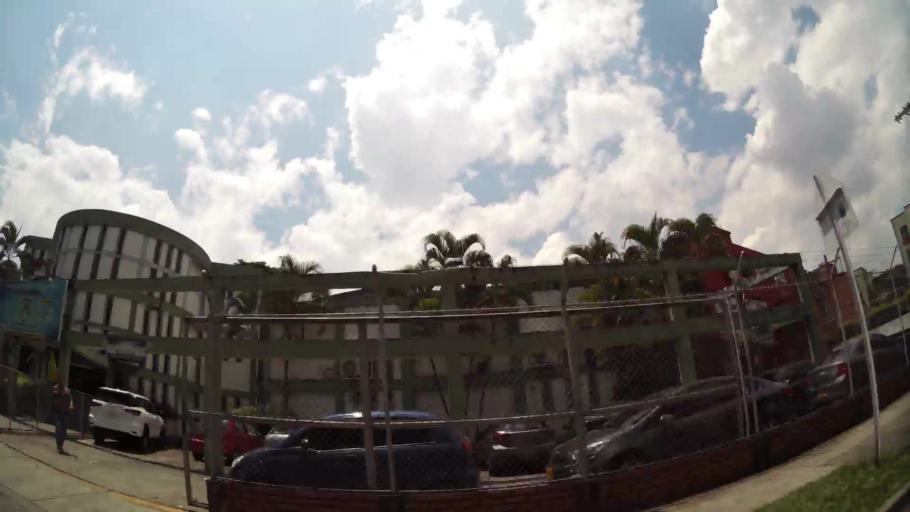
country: CO
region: Valle del Cauca
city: Cali
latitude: 3.4245
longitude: -76.5295
